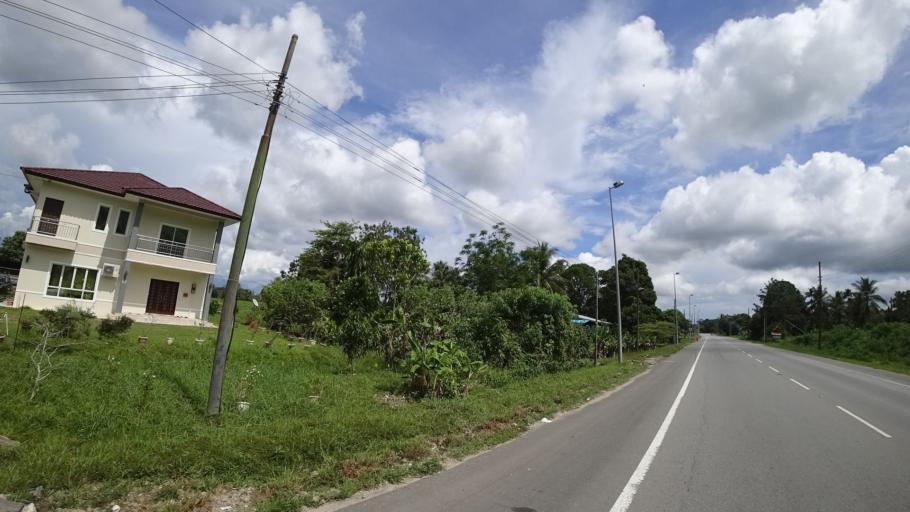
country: BN
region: Tutong
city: Tutong
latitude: 4.7536
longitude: 114.8185
